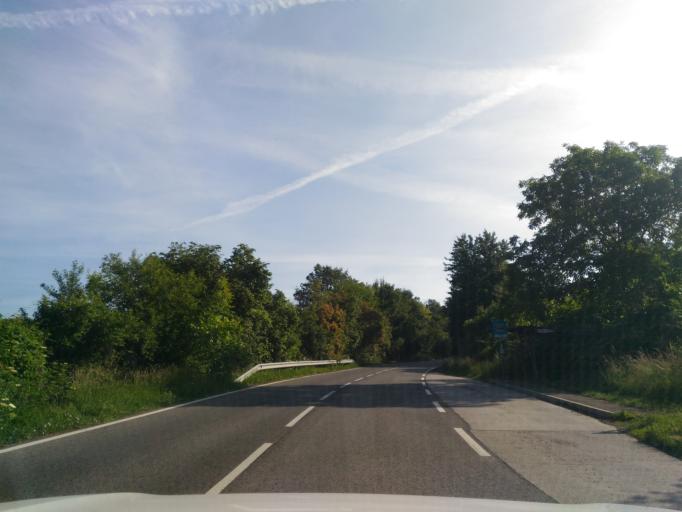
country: HU
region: Baranya
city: Komlo
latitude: 46.1705
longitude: 18.2607
